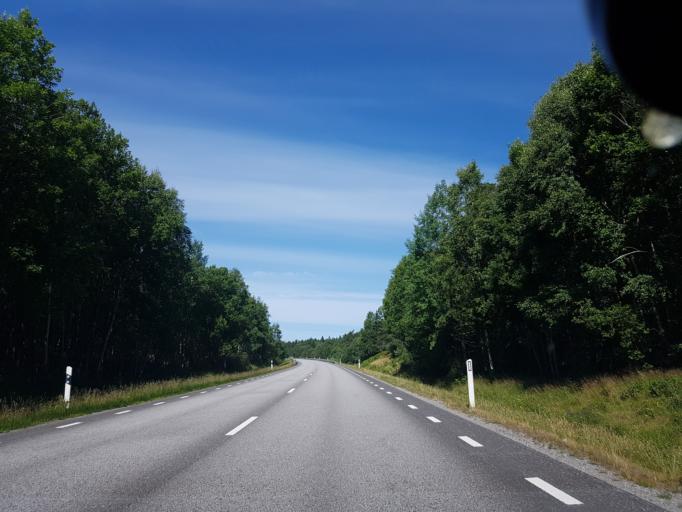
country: SE
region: Vaestra Goetaland
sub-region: Lysekils Kommun
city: Lysekil
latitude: 58.1559
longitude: 11.5213
